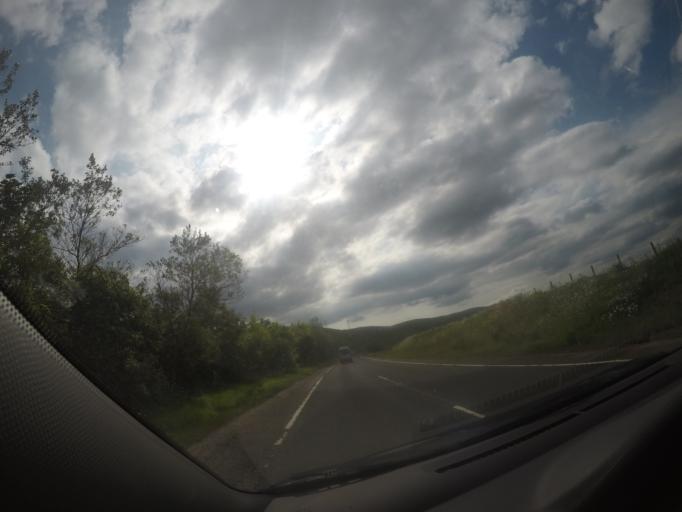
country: GB
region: Scotland
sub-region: South Lanarkshire
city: Douglas
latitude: 55.4671
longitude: -3.6727
